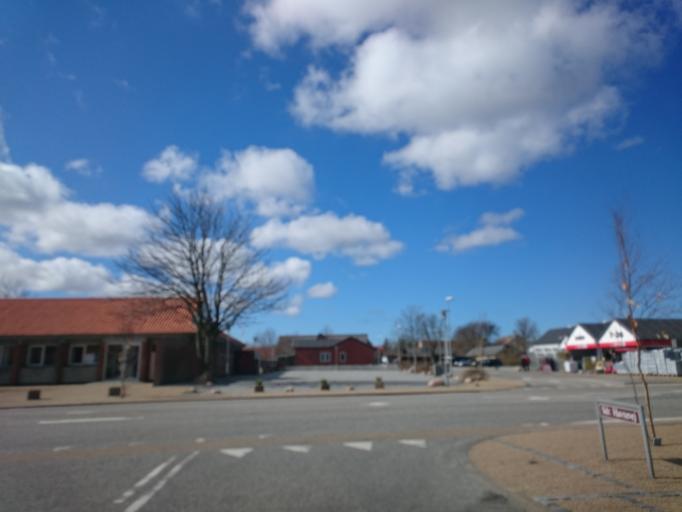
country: DK
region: North Denmark
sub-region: Frederikshavn Kommune
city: Strandby
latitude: 57.5927
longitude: 10.4129
